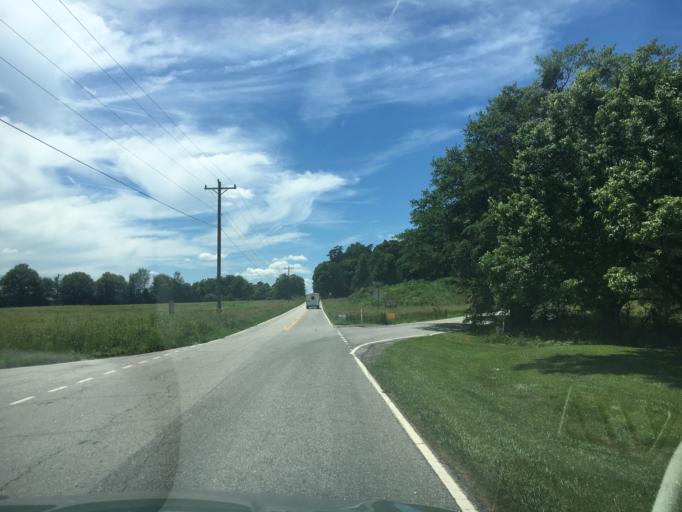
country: US
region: South Carolina
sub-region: Spartanburg County
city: Duncan
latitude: 34.8608
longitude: -82.1308
